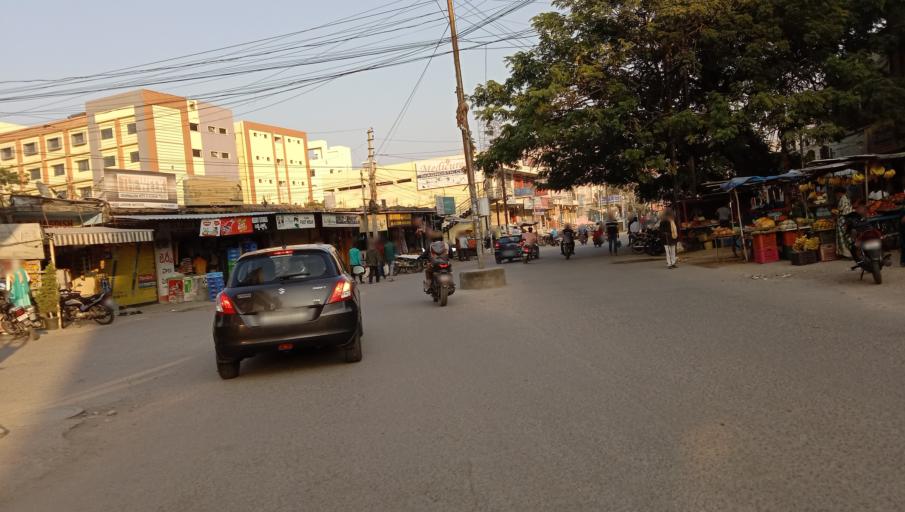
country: IN
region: Telangana
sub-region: Hyderabad
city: Hyderabad
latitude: 17.3643
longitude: 78.4263
